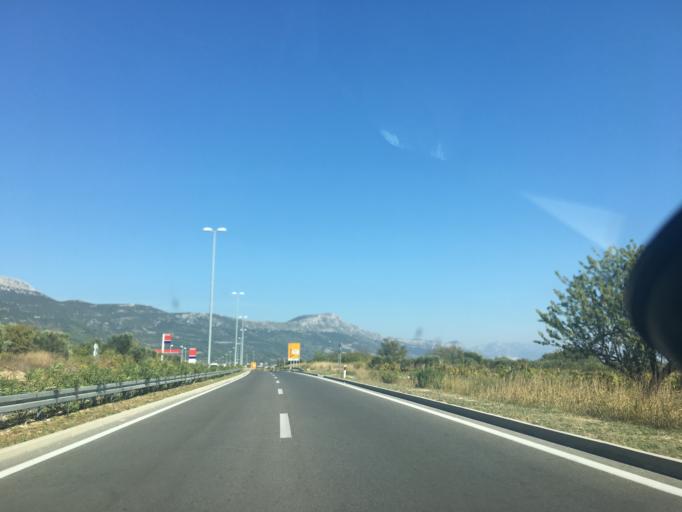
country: HR
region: Splitsko-Dalmatinska
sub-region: Grad Trogir
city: Trogir
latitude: 43.5512
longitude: 16.3138
